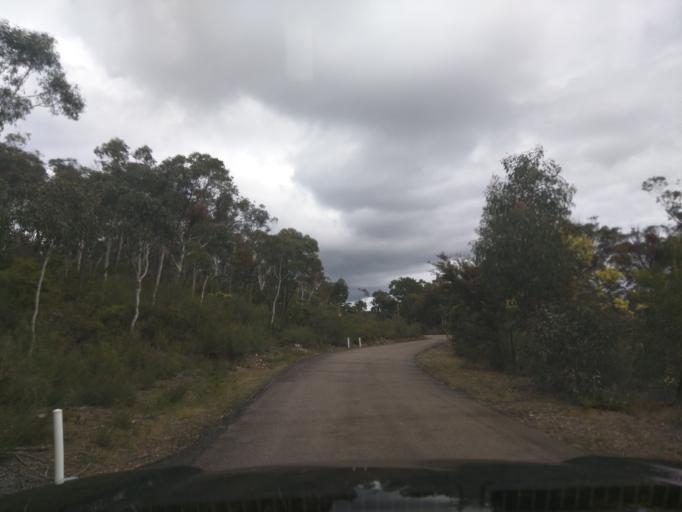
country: AU
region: New South Wales
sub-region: Wollongong
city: Mount Keira
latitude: -34.3308
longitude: 150.7451
